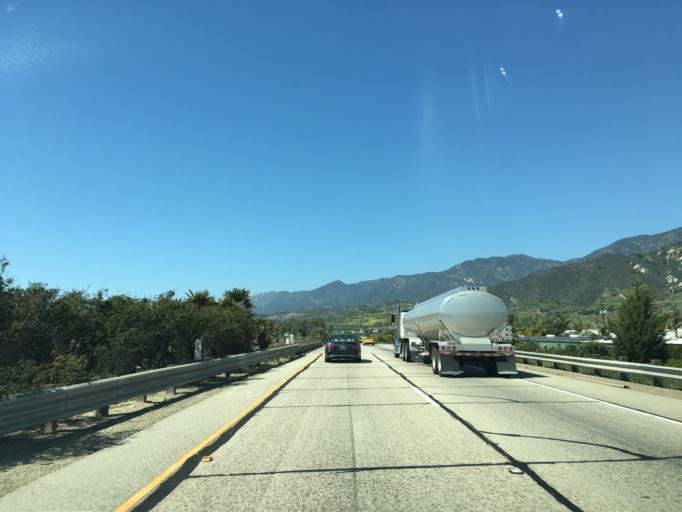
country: US
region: California
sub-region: Santa Barbara County
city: Toro Canyon
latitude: 34.4105
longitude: -119.5524
